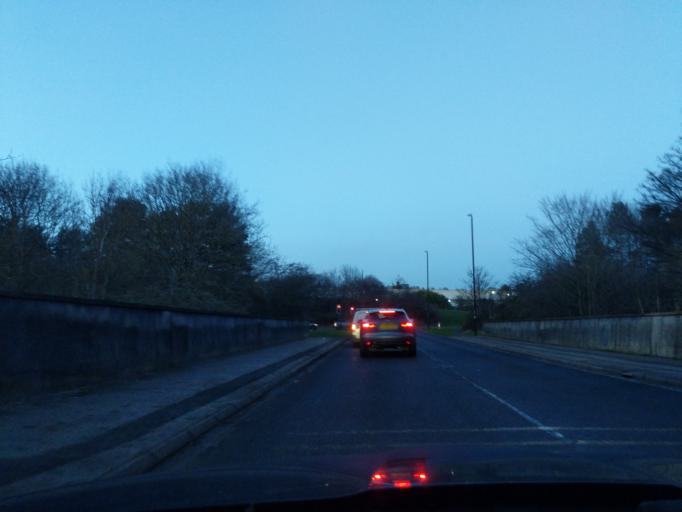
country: GB
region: England
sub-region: County Durham
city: Chester-le-Street
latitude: 54.8821
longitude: -1.5573
